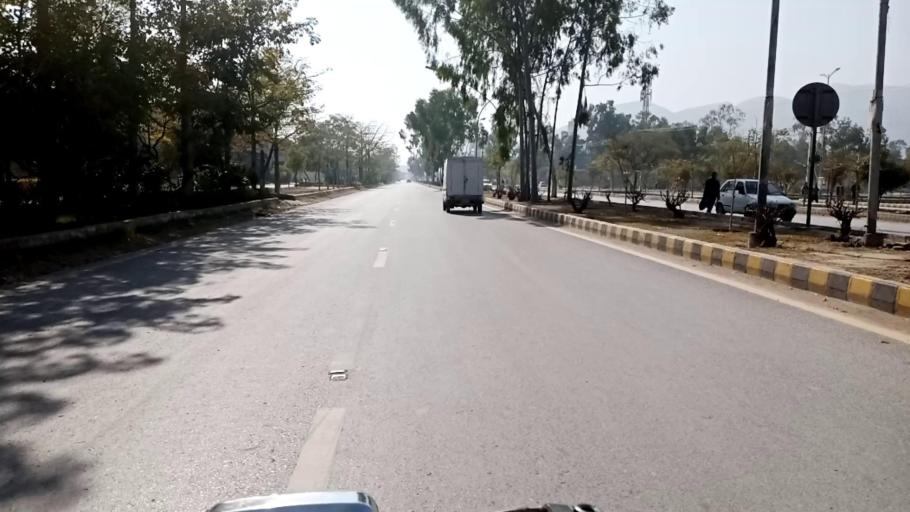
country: PK
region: Khyber Pakhtunkhwa
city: Peshawar
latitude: 33.9560
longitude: 71.4330
